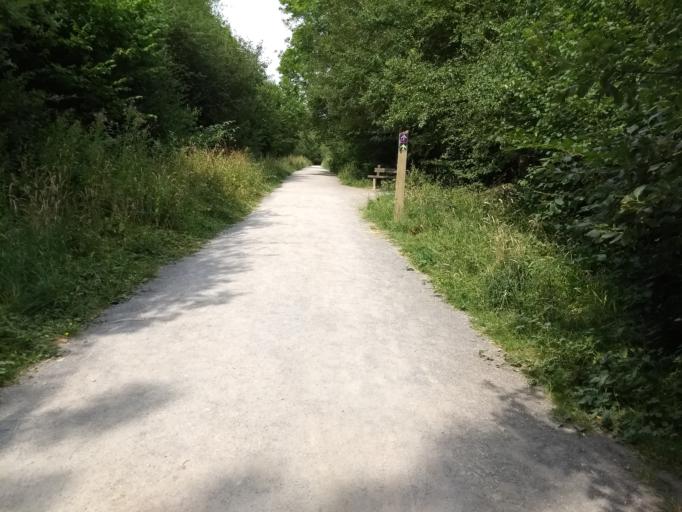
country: GB
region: England
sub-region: Northamptonshire
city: Hartwell
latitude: 52.1595
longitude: -0.8383
